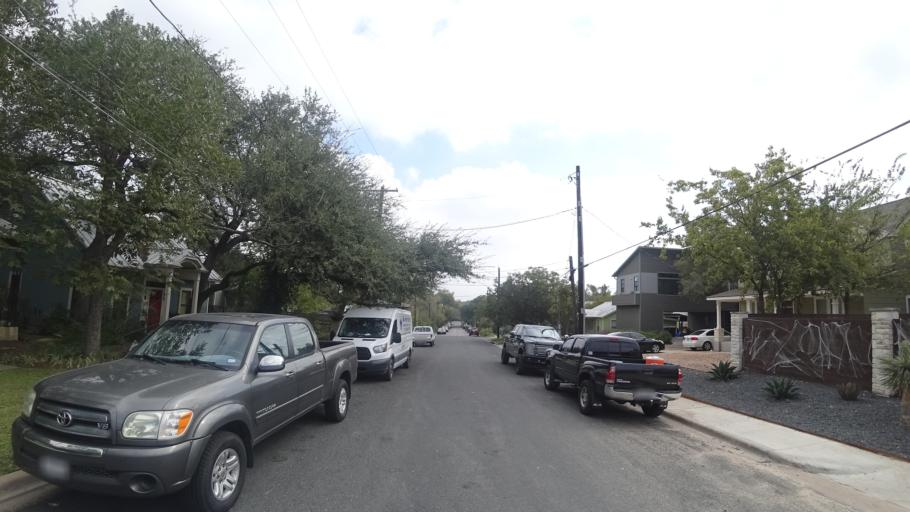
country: US
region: Texas
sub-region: Travis County
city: Austin
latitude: 30.2519
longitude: -97.7571
